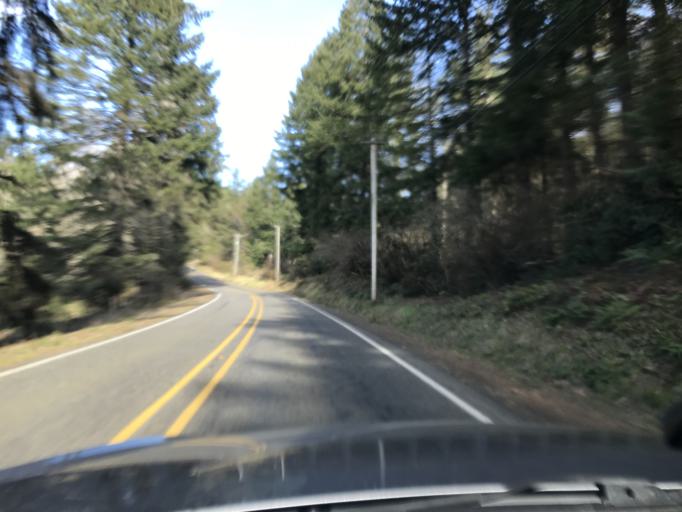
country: US
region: Washington
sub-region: Pierce County
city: Home
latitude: 47.2456
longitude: -122.7765
